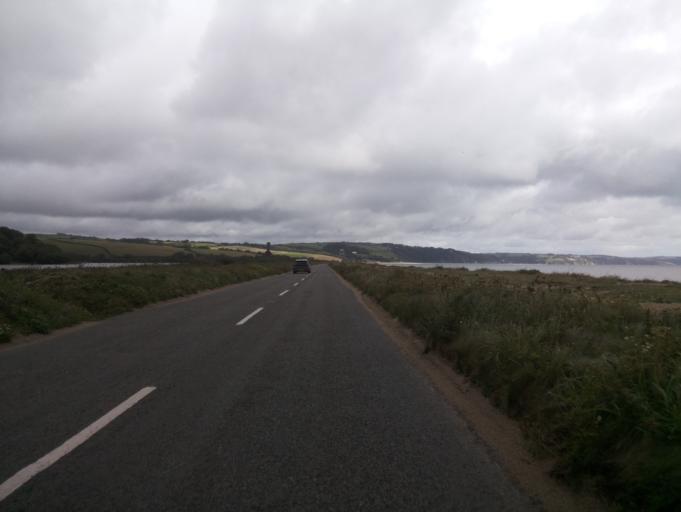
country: GB
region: England
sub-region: Devon
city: Dartmouth
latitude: 50.2766
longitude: -3.6495
